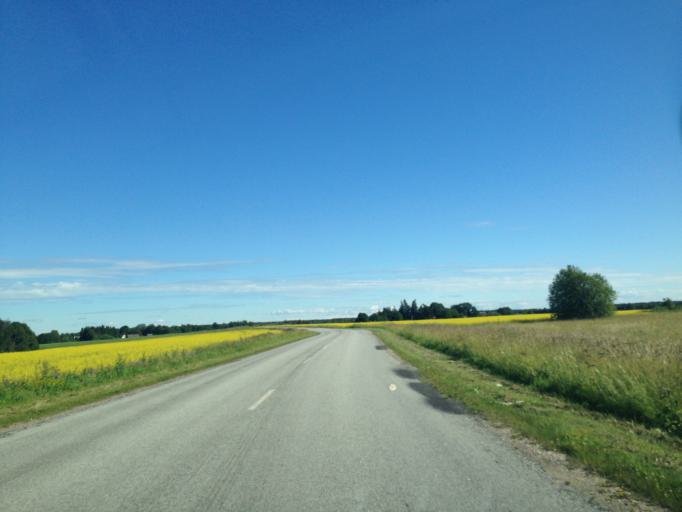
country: EE
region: Harju
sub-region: Kuusalu vald
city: Kuusalu
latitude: 59.4558
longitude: 25.3634
